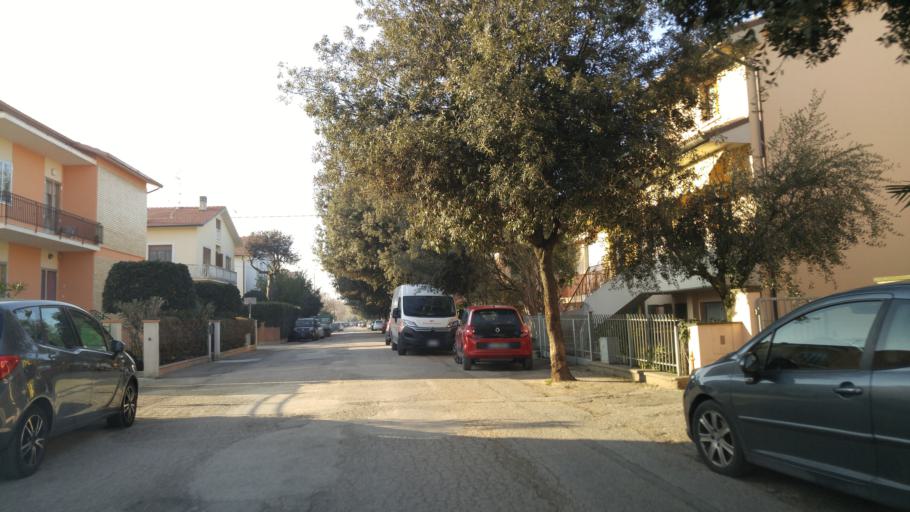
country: IT
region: The Marches
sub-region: Provincia di Pesaro e Urbino
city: Fano
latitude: 43.8556
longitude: 12.9986
